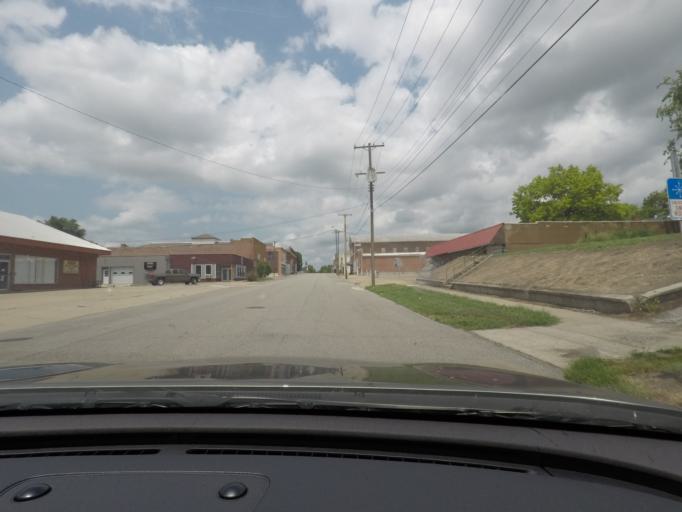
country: US
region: Missouri
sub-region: Carroll County
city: Carrollton
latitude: 39.3561
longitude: -93.4960
